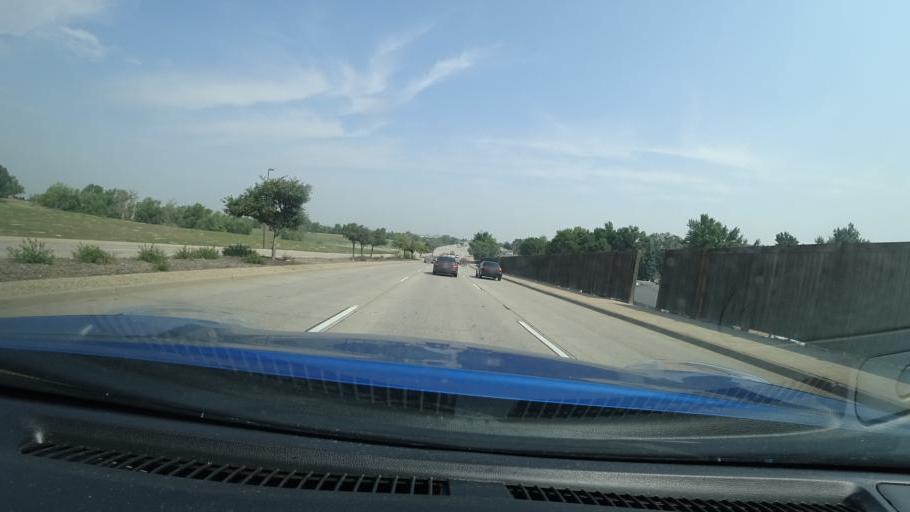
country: US
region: Colorado
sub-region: Adams County
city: Aurora
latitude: 39.7421
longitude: -104.7913
